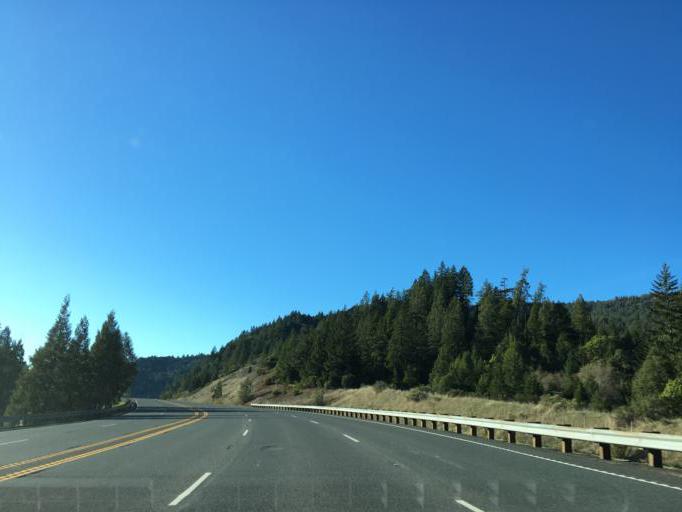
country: US
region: California
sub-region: Mendocino County
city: Laytonville
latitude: 39.8347
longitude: -123.6317
